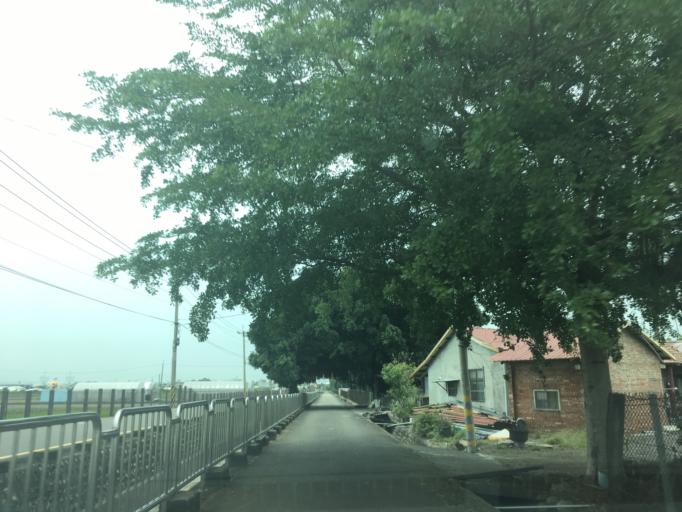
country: TW
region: Taiwan
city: Zhongxing New Village
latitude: 24.0322
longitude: 120.6891
